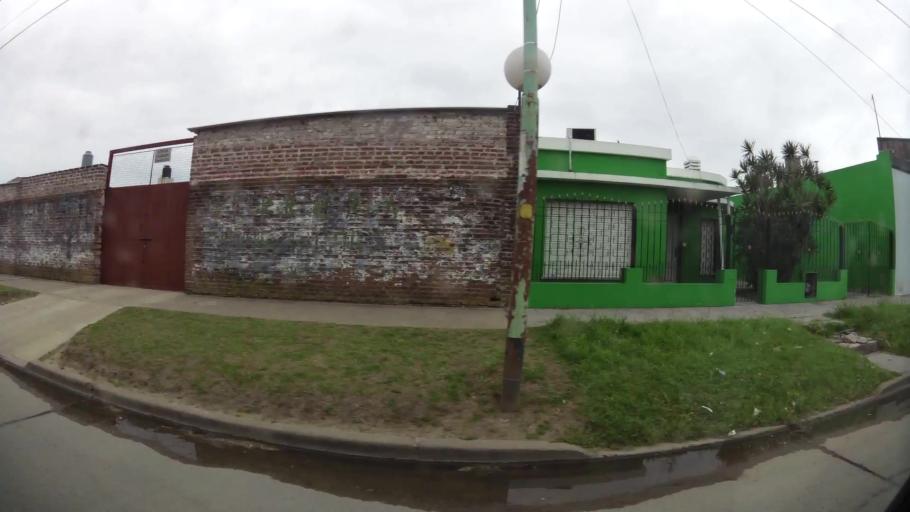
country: AR
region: Buenos Aires
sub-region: Partido de Zarate
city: Zarate
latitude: -34.1088
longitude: -59.0233
